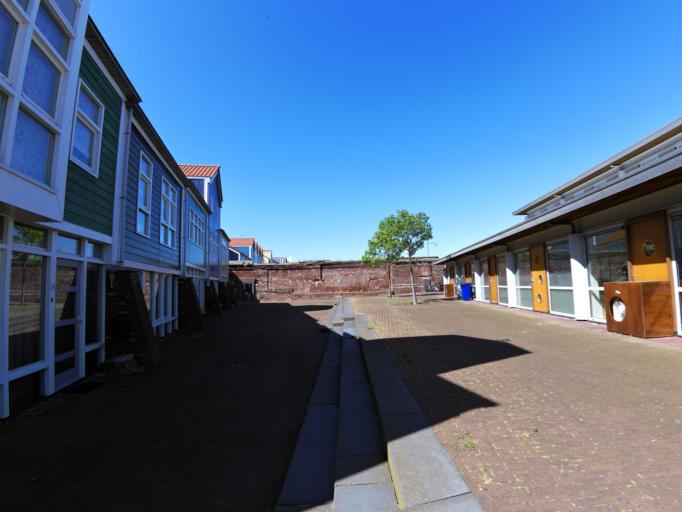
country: NL
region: South Holland
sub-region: Gemeente Hellevoetsluis
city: Hellevoetsluis
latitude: 51.8245
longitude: 4.1275
